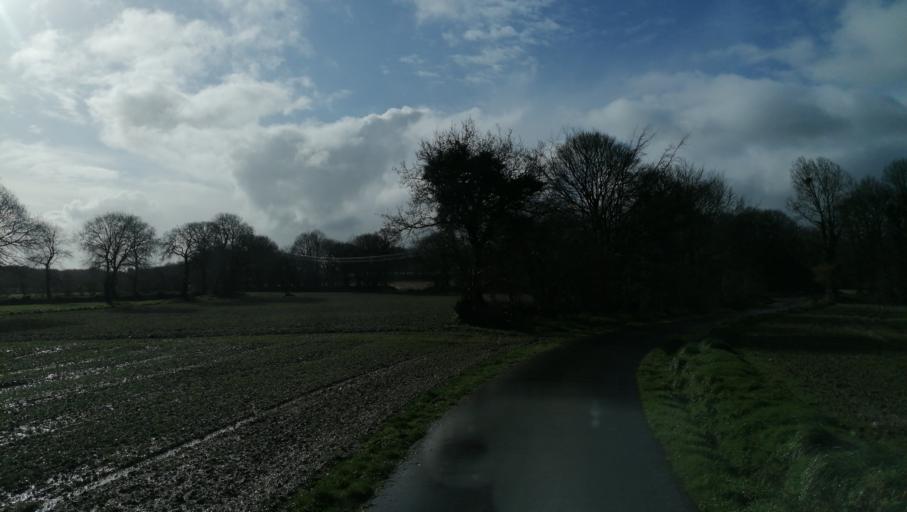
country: FR
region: Brittany
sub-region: Departement des Cotes-d'Armor
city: Lanrodec
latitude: 48.4840
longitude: -3.0195
